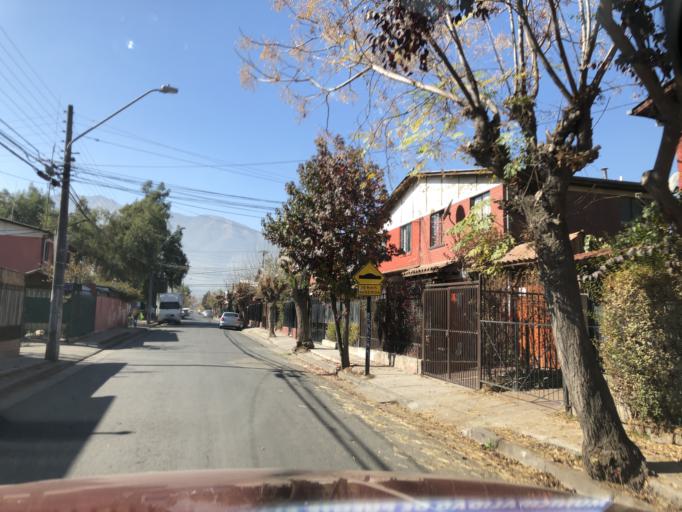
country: CL
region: Santiago Metropolitan
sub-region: Provincia de Cordillera
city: Puente Alto
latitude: -33.5657
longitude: -70.5780
